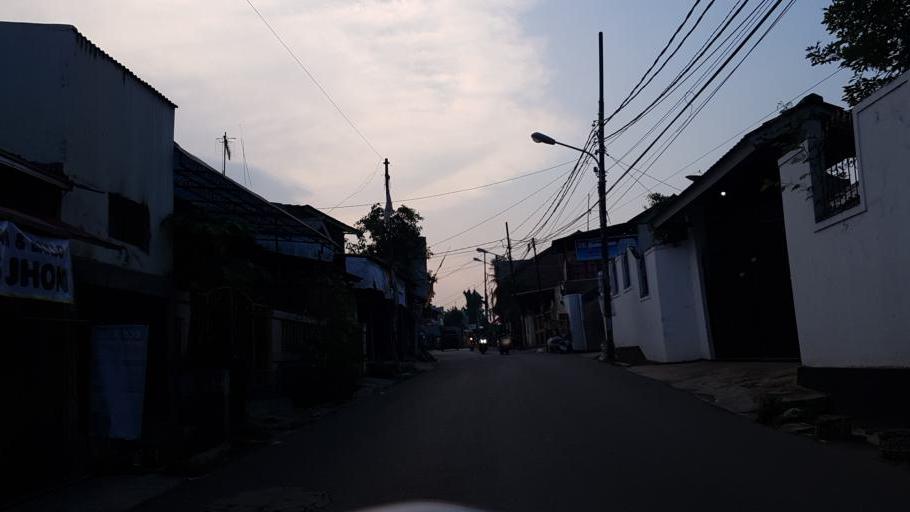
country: ID
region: West Java
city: Bekasi
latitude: -6.2658
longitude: 106.9471
